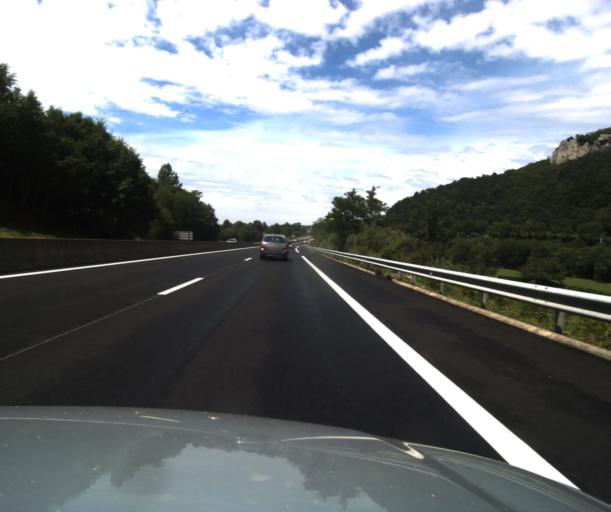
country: FR
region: Midi-Pyrenees
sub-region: Departement des Hautes-Pyrenees
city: Lourdes
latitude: 43.0778
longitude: -0.0439
